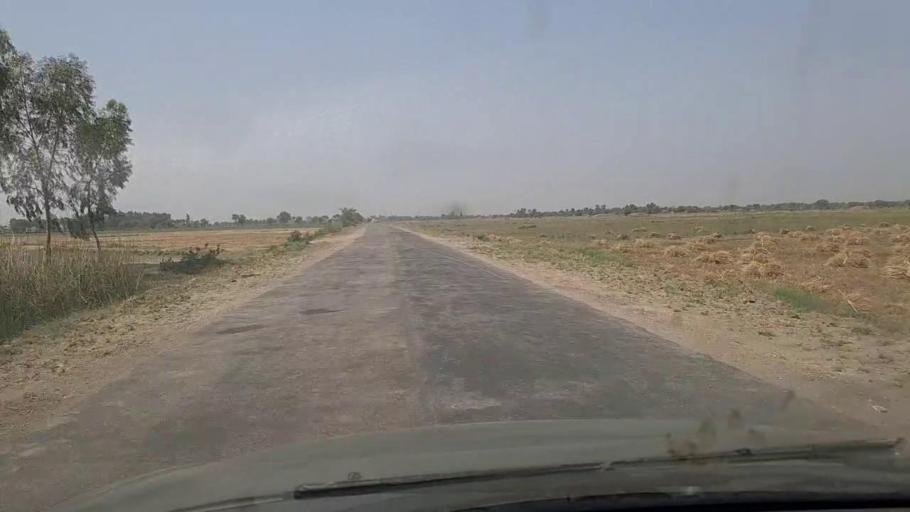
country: PK
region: Sindh
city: Khanpur
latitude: 27.8627
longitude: 69.4388
